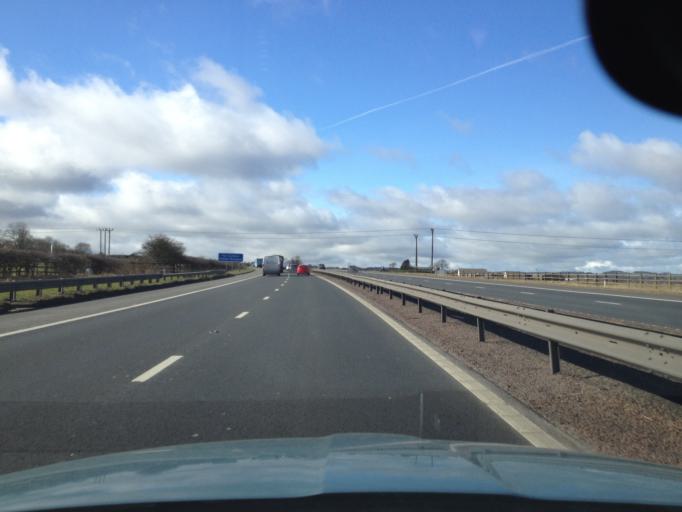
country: GB
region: Scotland
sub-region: West Lothian
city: Broxburn
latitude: 55.9263
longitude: -3.4496
